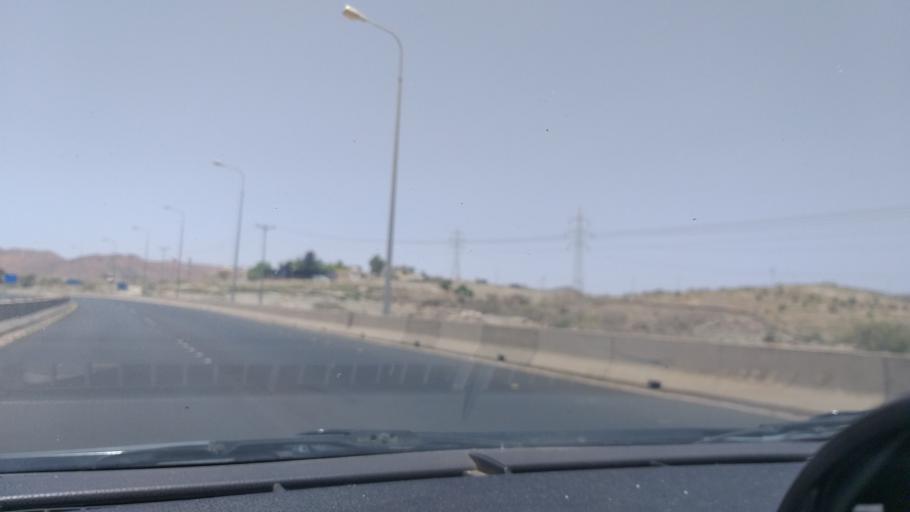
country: SA
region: Makkah
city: Al Hada
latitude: 21.3412
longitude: 40.3403
